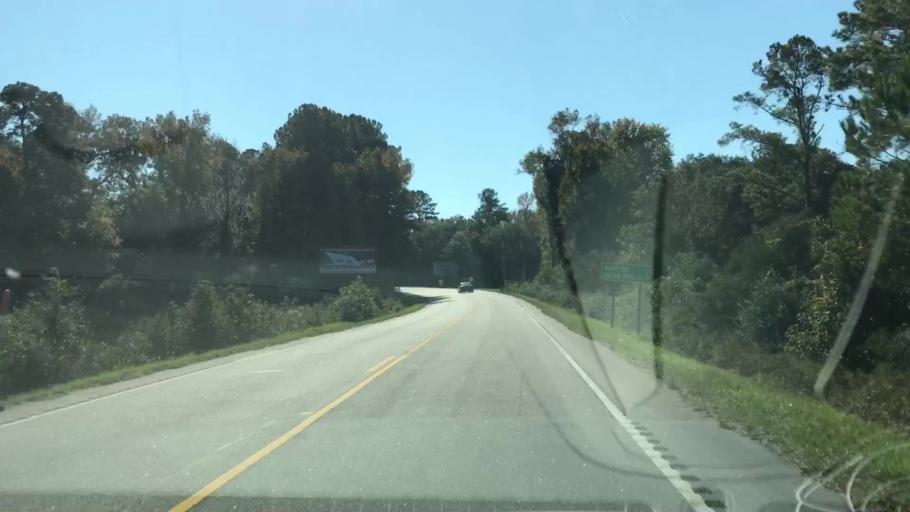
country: US
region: South Carolina
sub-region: Jasper County
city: Ridgeland
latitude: 32.5420
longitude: -80.9122
